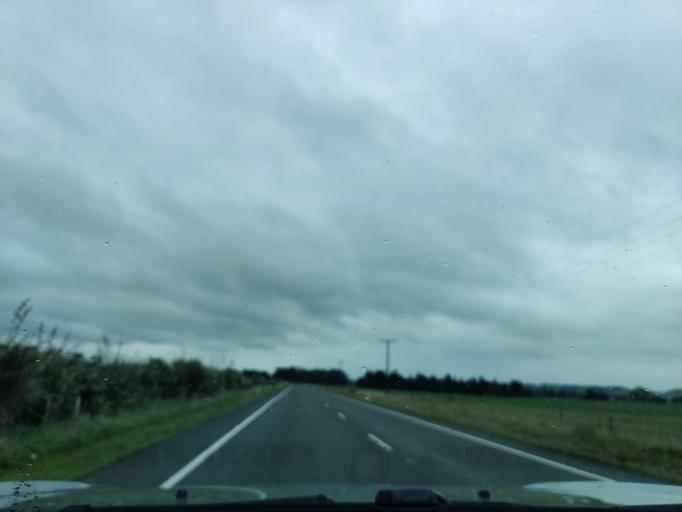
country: NZ
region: Hawke's Bay
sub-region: Hastings District
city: Hastings
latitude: -40.0005
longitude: 176.4001
